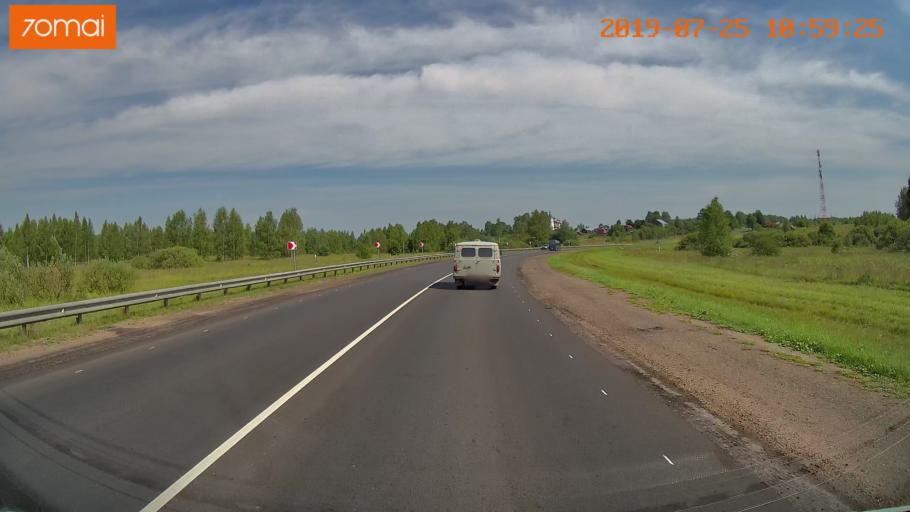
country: RU
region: Ivanovo
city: Furmanov
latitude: 57.1779
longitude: 41.0842
